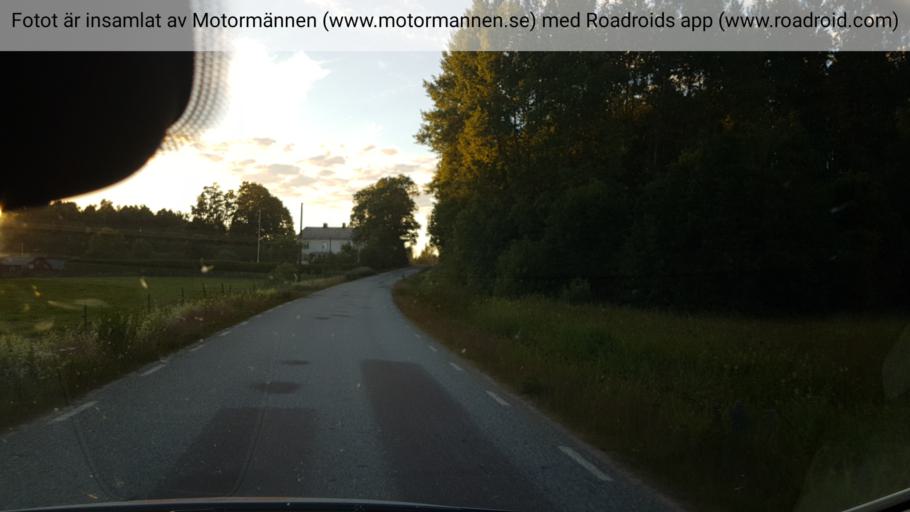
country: SE
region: Vaermland
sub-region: Sunne Kommun
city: Sunne
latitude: 59.6695
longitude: 12.9054
